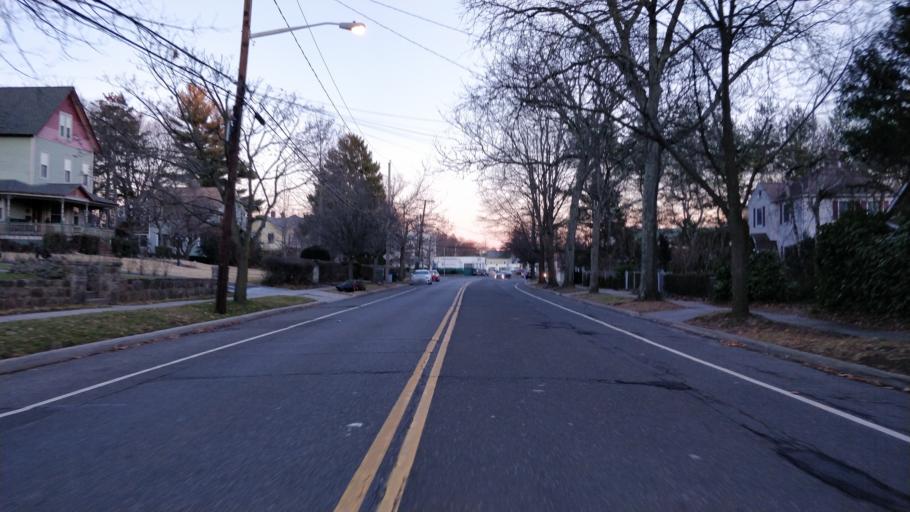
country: US
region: New York
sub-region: Nassau County
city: Sea Cliff
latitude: 40.8502
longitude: -73.6371
